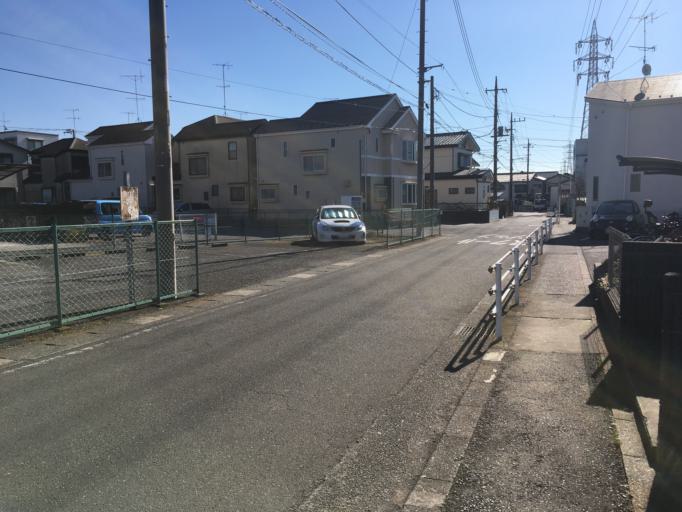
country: JP
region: Kanagawa
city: Minami-rinkan
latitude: 35.4629
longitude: 139.4686
